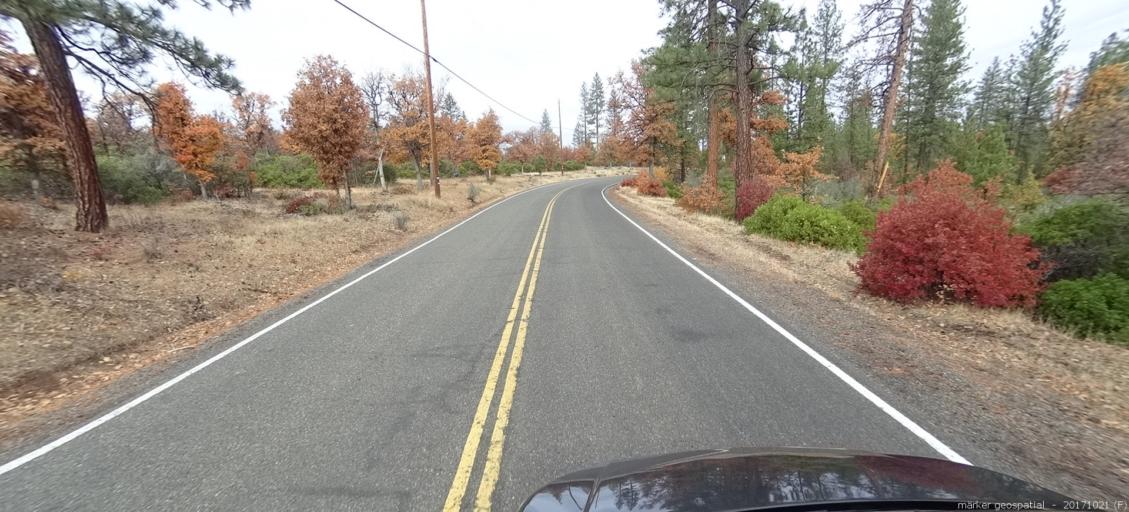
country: US
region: California
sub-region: Shasta County
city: Burney
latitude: 40.9342
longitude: -121.5685
